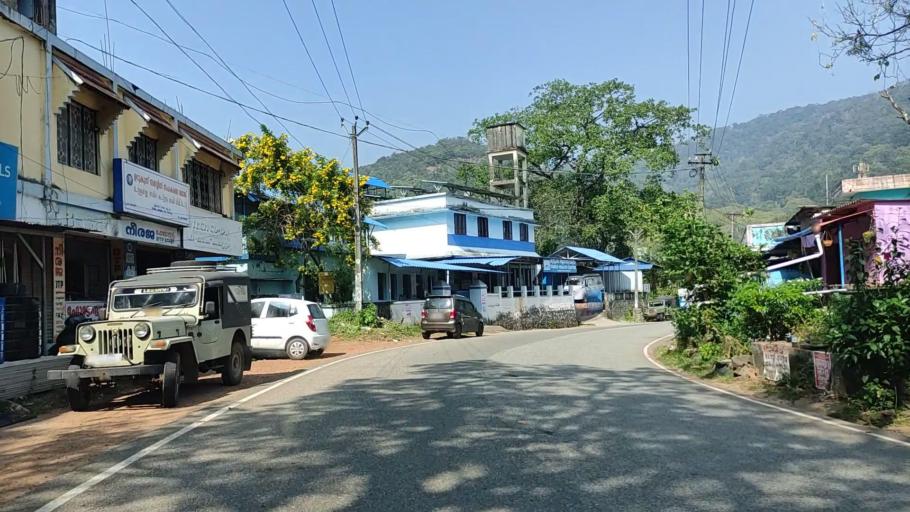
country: IN
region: Kerala
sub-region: Kollam
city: Punalur
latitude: 8.9663
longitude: 77.0689
